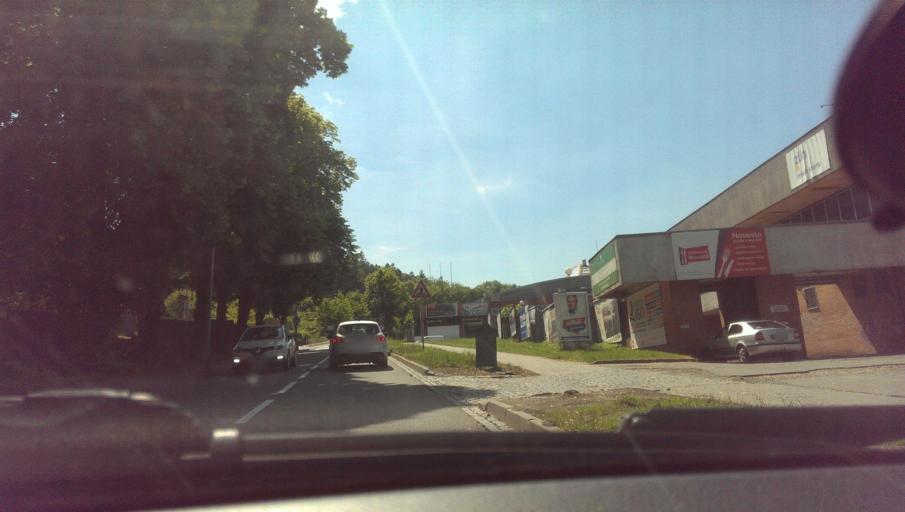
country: CZ
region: Zlin
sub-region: Okres Zlin
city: Zlin
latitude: 49.2190
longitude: 17.6601
